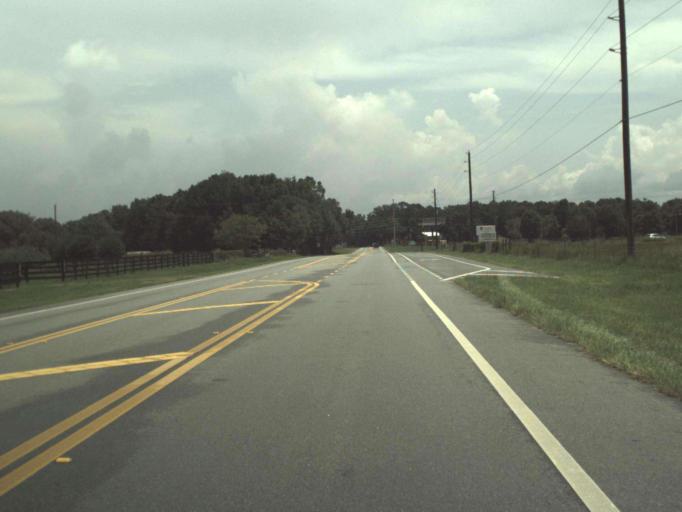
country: US
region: Florida
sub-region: Sumter County
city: Lake Panasoffkee
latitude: 28.7377
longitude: -82.0676
